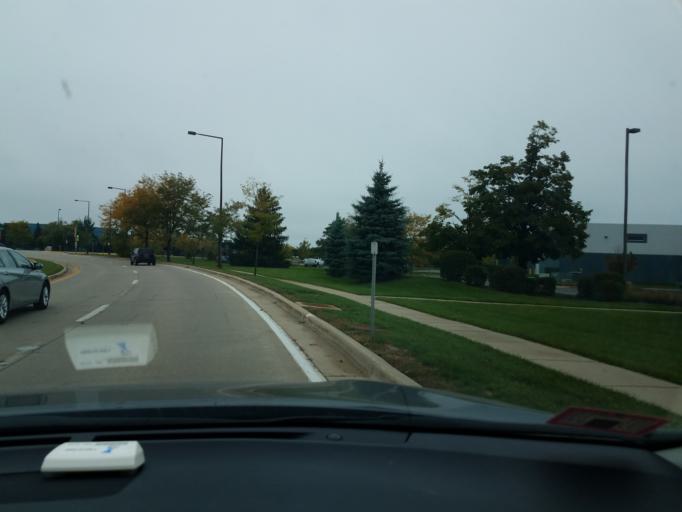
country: US
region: Illinois
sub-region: Cook County
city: Buffalo Grove
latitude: 42.1702
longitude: -87.9395
